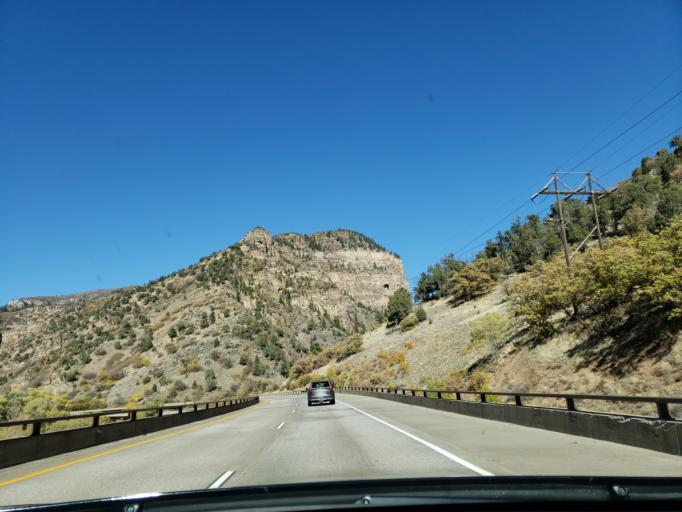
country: US
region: Colorado
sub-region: Garfield County
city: Glenwood Springs
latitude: 39.5594
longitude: -107.2478
